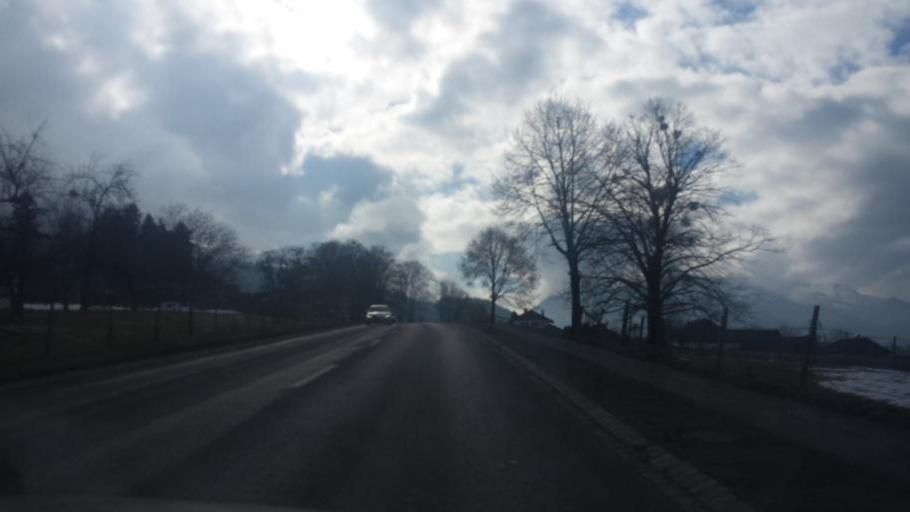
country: DE
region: Bavaria
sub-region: Upper Bavaria
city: Benediktbeuern
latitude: 47.6779
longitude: 11.3993
